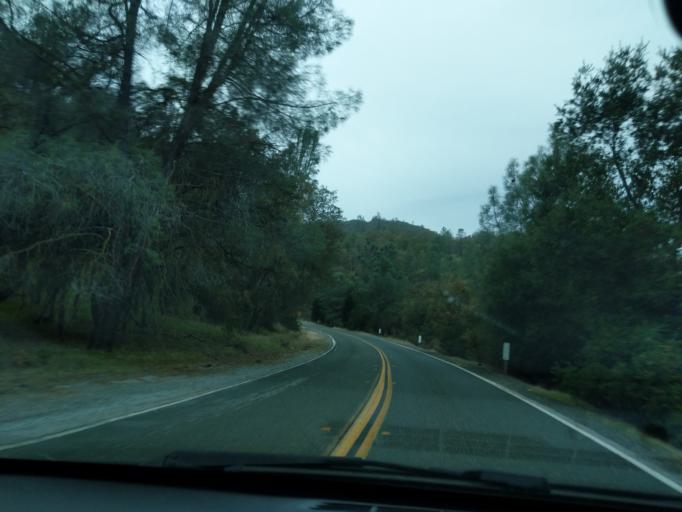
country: US
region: California
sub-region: Monterey County
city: Soledad
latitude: 36.5919
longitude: -121.1964
